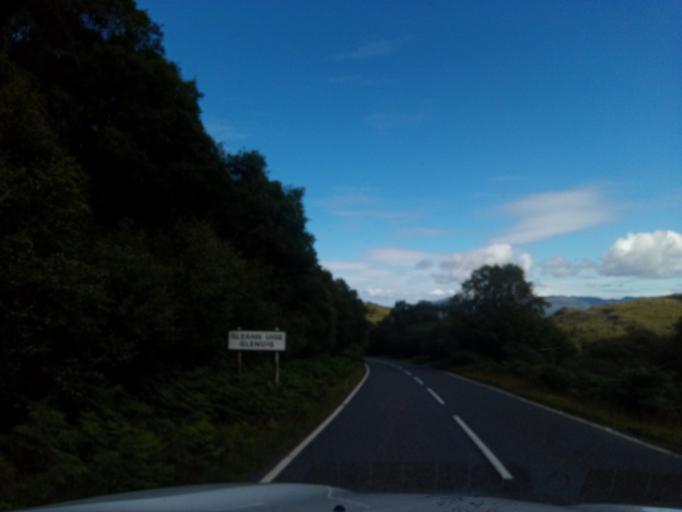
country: GB
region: Scotland
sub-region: Argyll and Bute
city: Isle Of Mull
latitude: 56.8151
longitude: -5.8208
